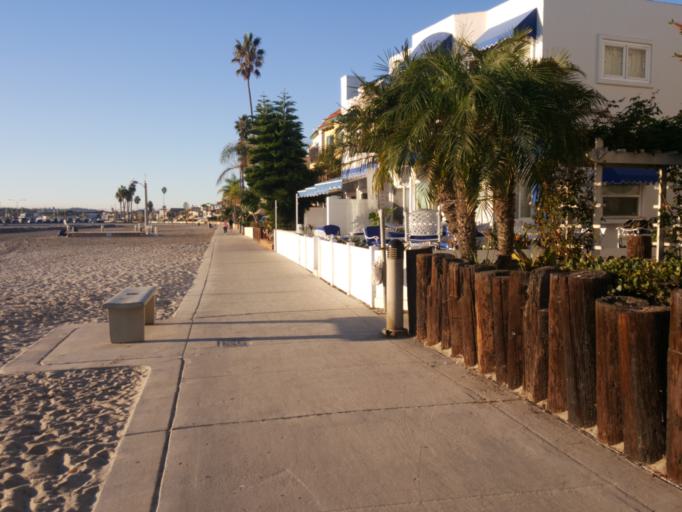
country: US
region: California
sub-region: San Diego County
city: La Jolla
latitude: 32.7811
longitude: -117.2513
